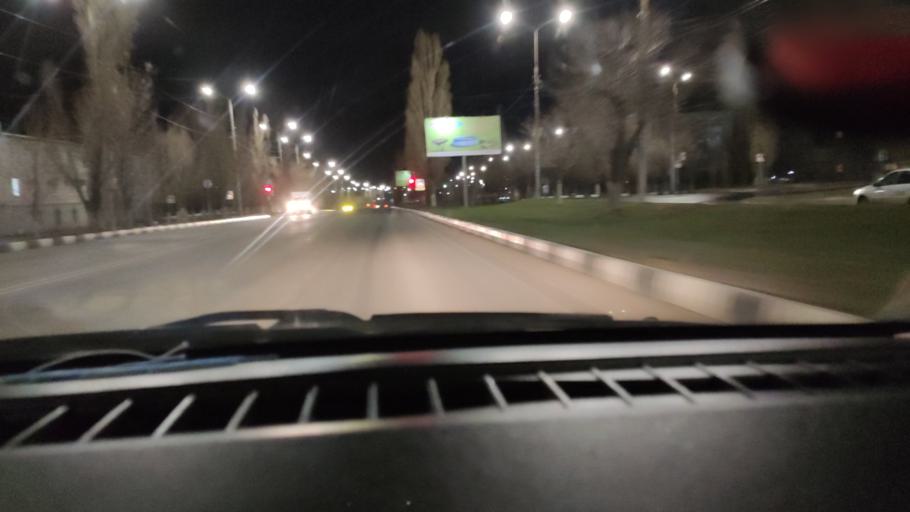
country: RU
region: Saratov
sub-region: Saratovskiy Rayon
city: Saratov
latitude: 51.6081
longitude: 45.9693
